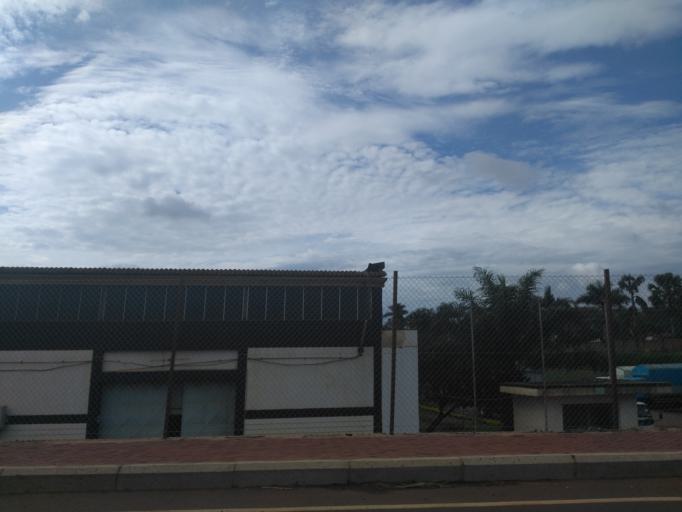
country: UG
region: Eastern Region
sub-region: Jinja District
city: Jinja
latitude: 0.4380
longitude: 33.1852
